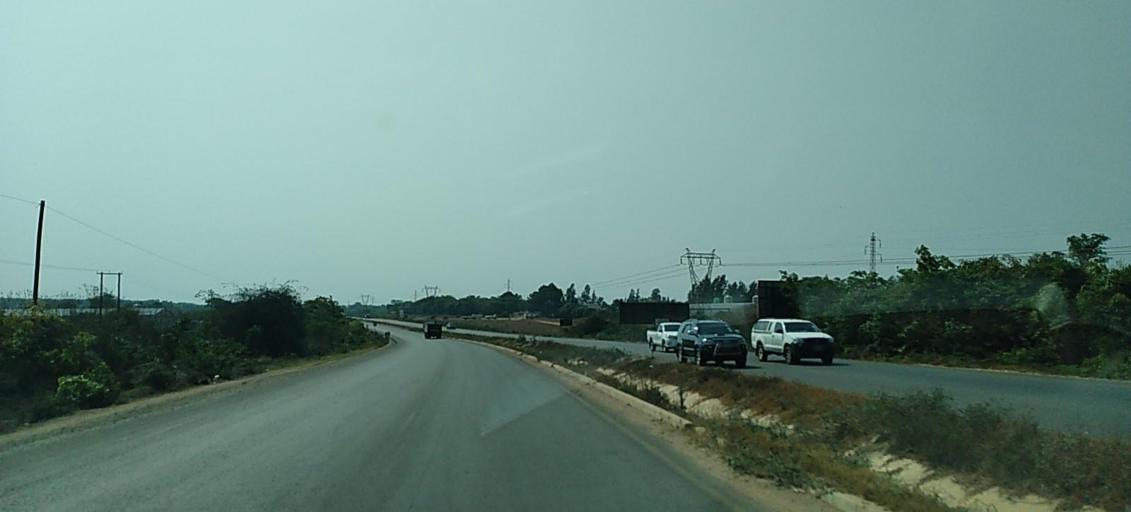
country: ZM
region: Copperbelt
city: Chingola
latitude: -12.5621
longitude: 27.8823
